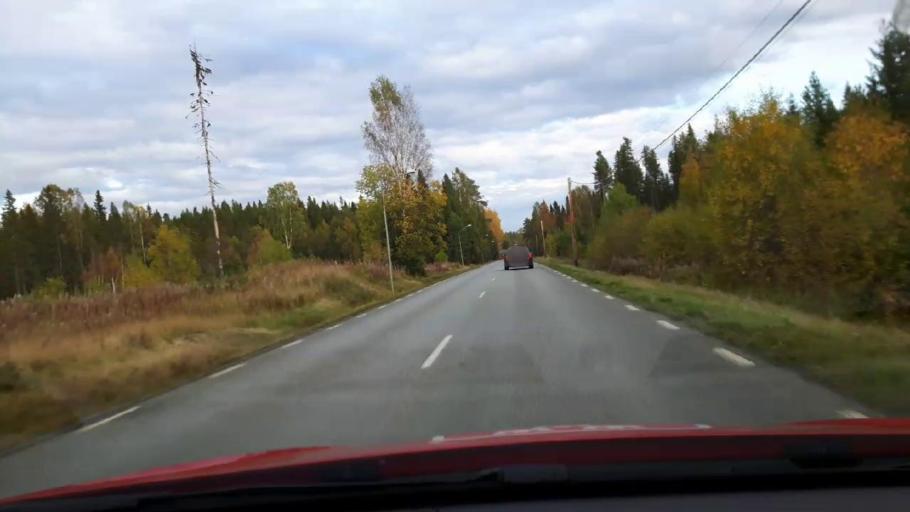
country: SE
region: Jaemtland
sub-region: Krokoms Kommun
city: Krokom
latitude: 63.3558
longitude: 14.5250
